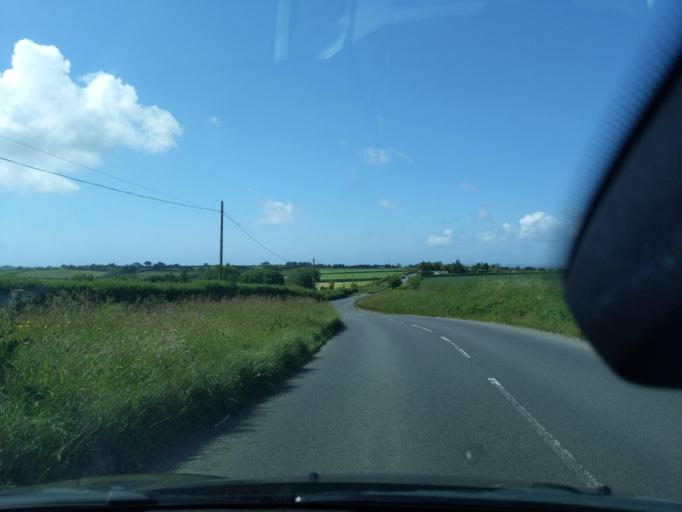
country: GB
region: England
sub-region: Devon
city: Great Torrington
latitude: 50.9941
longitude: -4.0962
